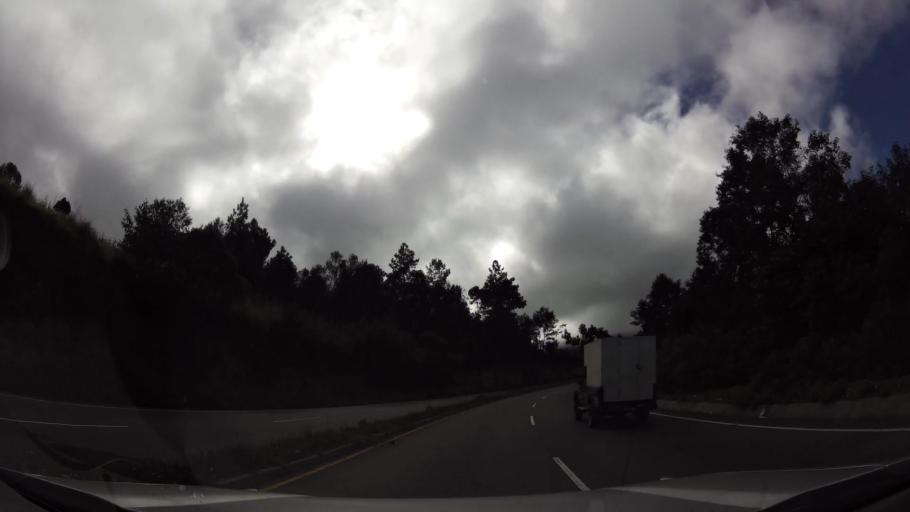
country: GT
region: Quetzaltenango
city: Salcaja
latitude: 14.8598
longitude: -91.4070
